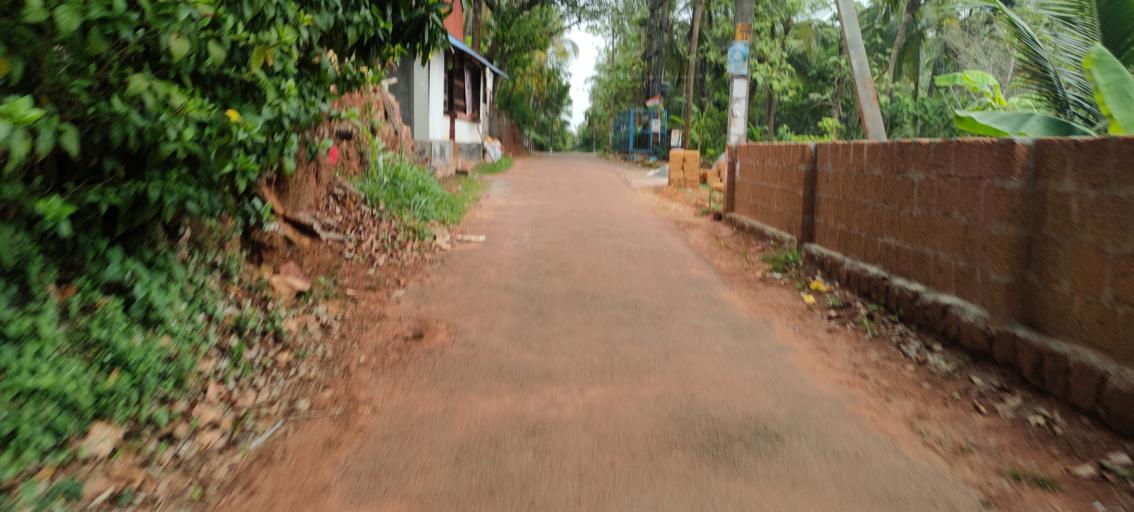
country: IN
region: Kerala
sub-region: Malappuram
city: Ponnani
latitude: 10.7711
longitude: 76.0315
